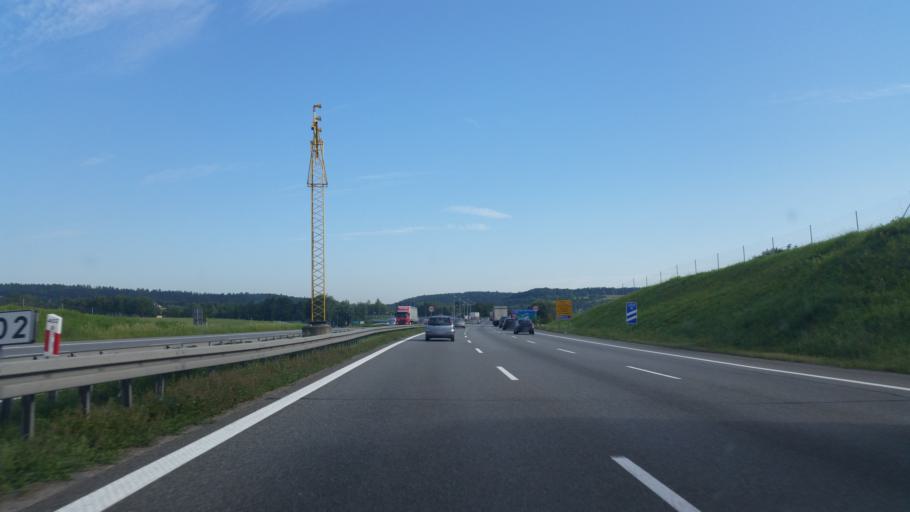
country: PL
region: Lesser Poland Voivodeship
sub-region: Powiat krakowski
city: Balice
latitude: 50.0806
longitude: 19.8083
